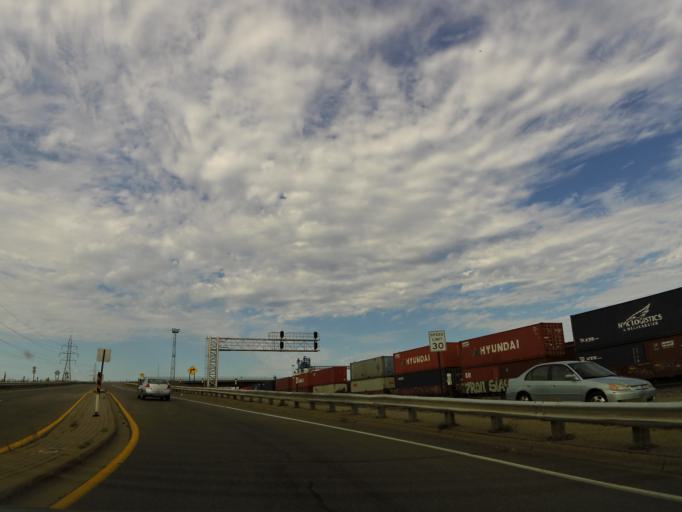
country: US
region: Minnesota
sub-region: Anoka County
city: Columbia Heights
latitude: 45.0431
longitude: -93.2744
